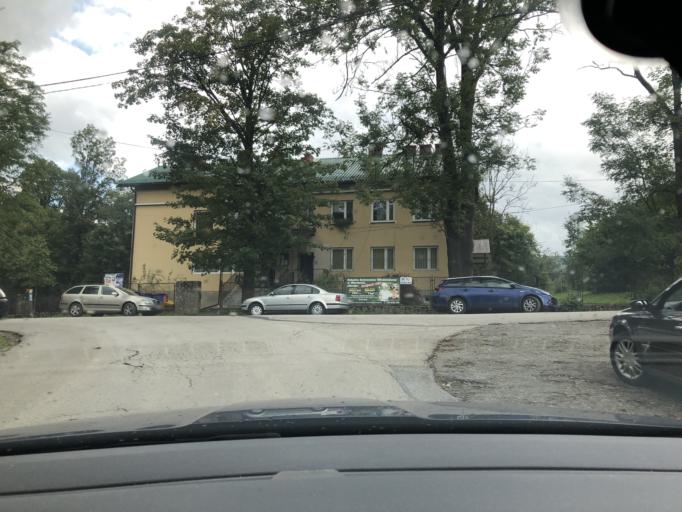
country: PL
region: Silesian Voivodeship
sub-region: Powiat zywiecki
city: Slemien
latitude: 49.7225
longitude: 19.3797
